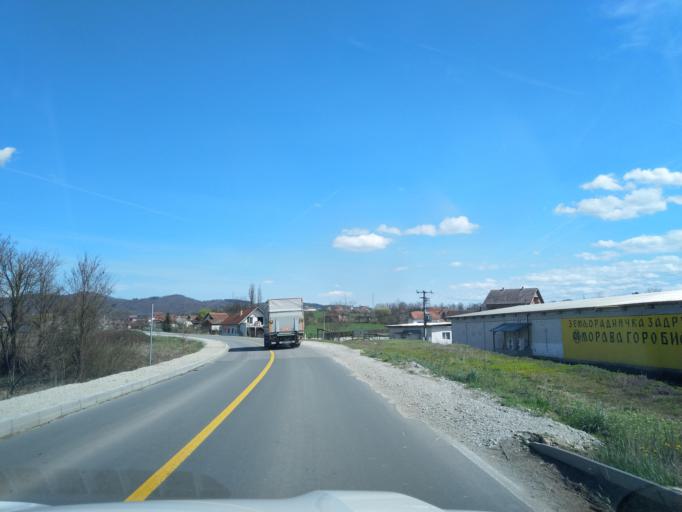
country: RS
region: Central Serbia
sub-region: Zlatiborski Okrug
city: Pozega
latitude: 43.8294
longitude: 20.0645
